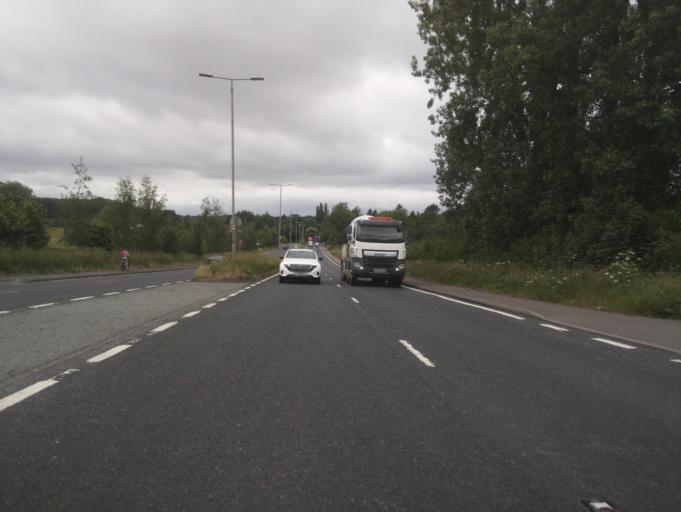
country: GB
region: England
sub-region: Leicestershire
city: Kirby Muxloe
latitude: 52.6657
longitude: -1.2346
